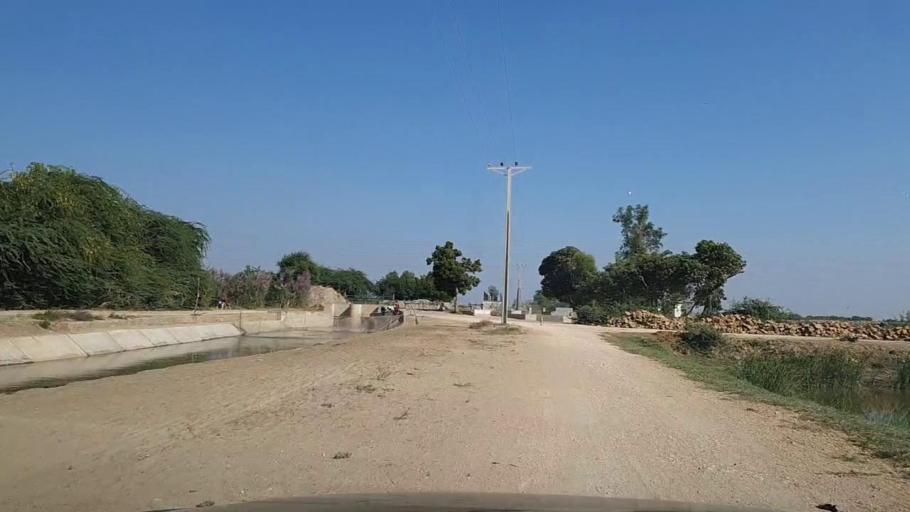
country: PK
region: Sindh
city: Thatta
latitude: 24.5960
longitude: 67.8190
